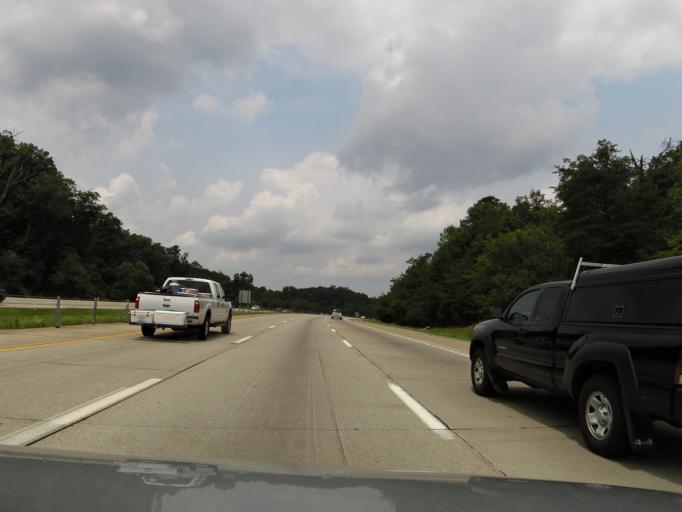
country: US
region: Kentucky
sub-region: Bullitt County
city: Shepherdsville
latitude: 37.9575
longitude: -85.6921
